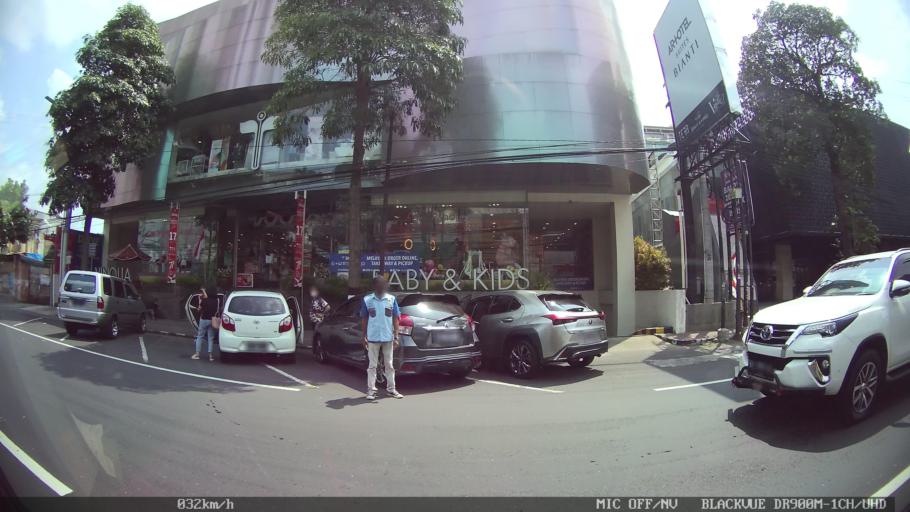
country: ID
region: Daerah Istimewa Yogyakarta
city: Yogyakarta
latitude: -7.7831
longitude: 110.3819
